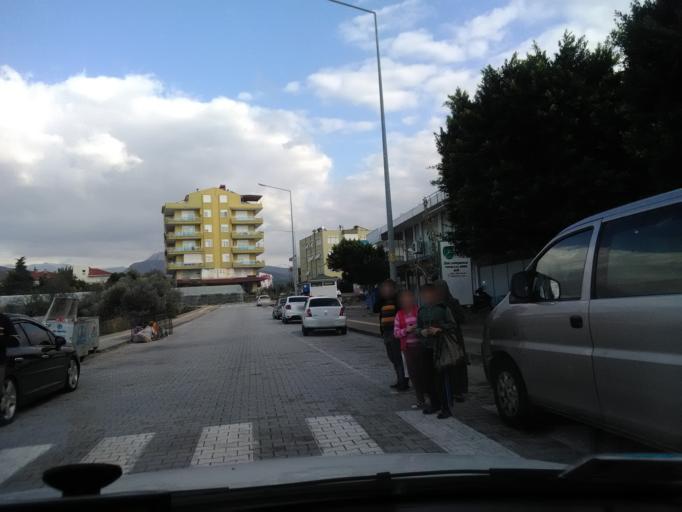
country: TR
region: Antalya
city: Gazipasa
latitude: 36.2693
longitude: 32.3192
